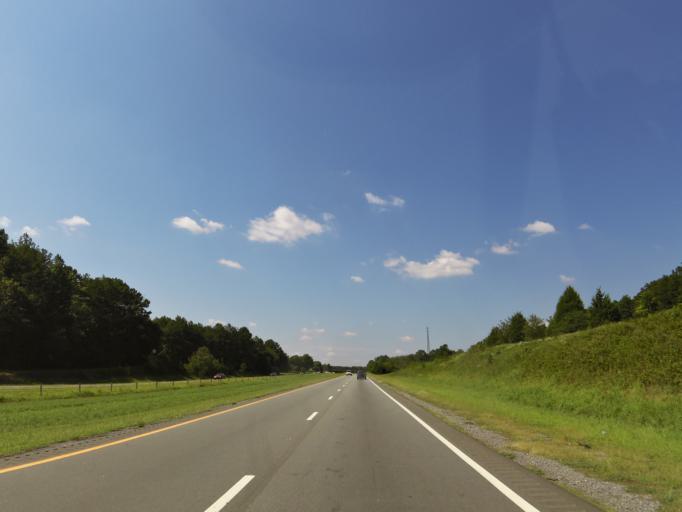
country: US
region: North Carolina
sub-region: Gaston County
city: Dallas
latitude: 35.3486
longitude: -81.1966
